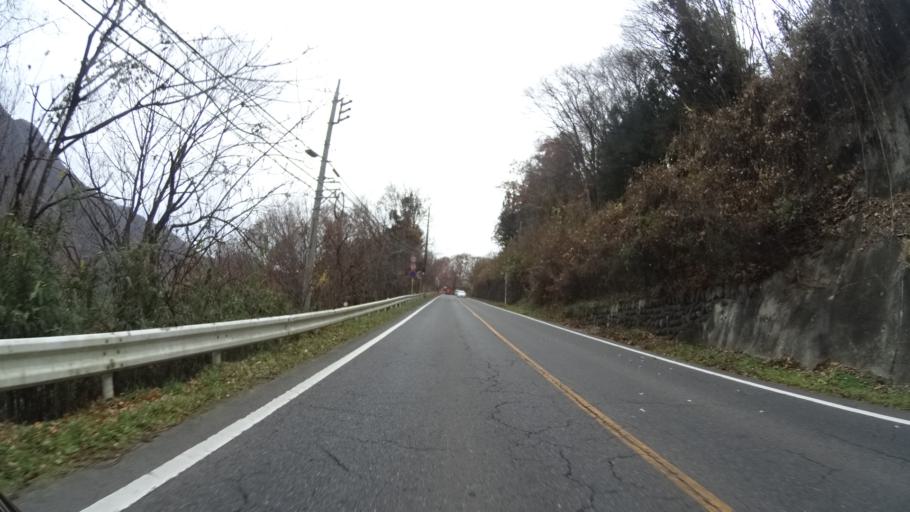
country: JP
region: Gunma
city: Numata
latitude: 36.6812
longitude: 139.2067
